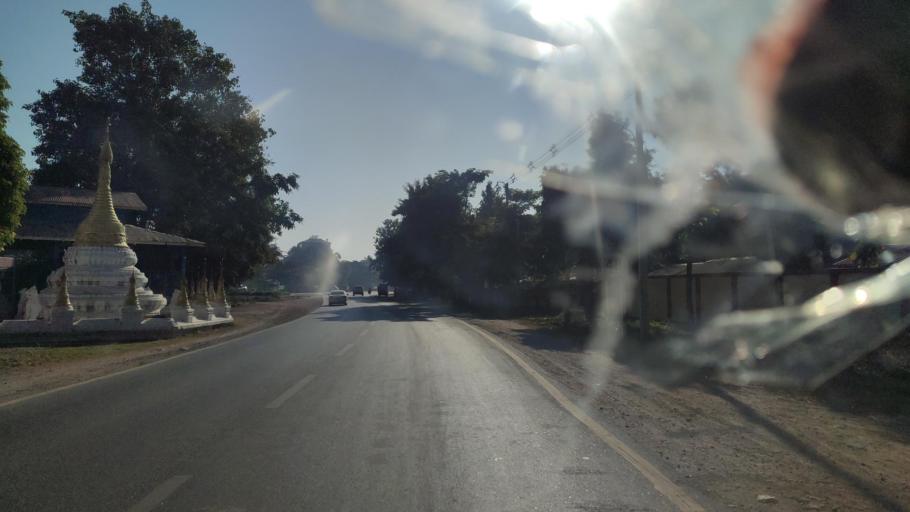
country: MM
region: Mandalay
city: Mandalay
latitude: 21.9075
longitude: 96.1797
